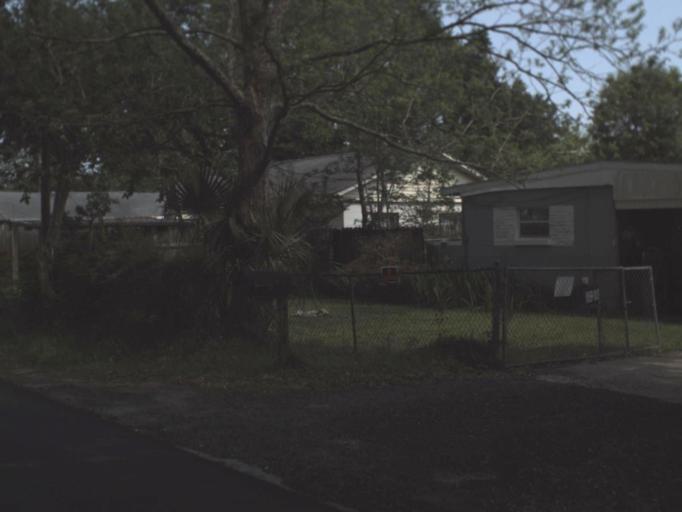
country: US
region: Florida
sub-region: Escambia County
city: West Pensacola
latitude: 30.4266
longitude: -87.2797
